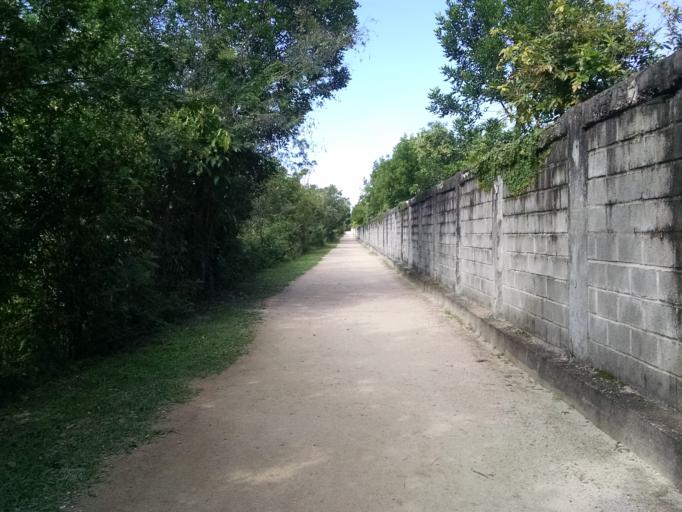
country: BR
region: Rio de Janeiro
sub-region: Sao Joao De Meriti
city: Sao Joao de Meriti
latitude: -22.9949
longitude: -43.3761
